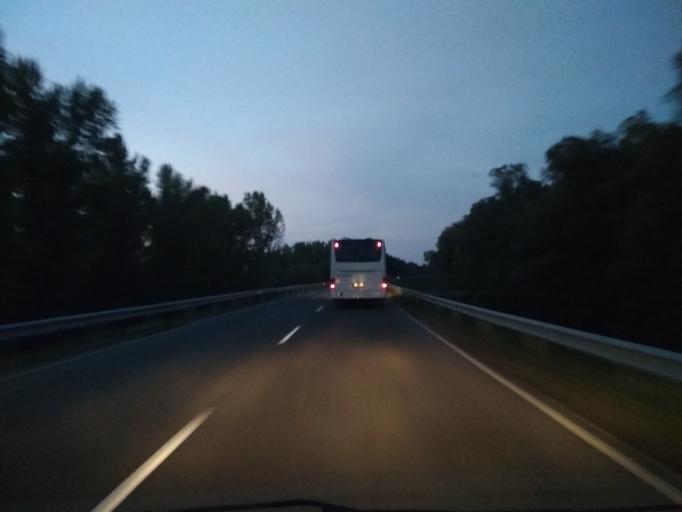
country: HU
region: Fejer
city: Adony
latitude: 47.1454
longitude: 18.8595
